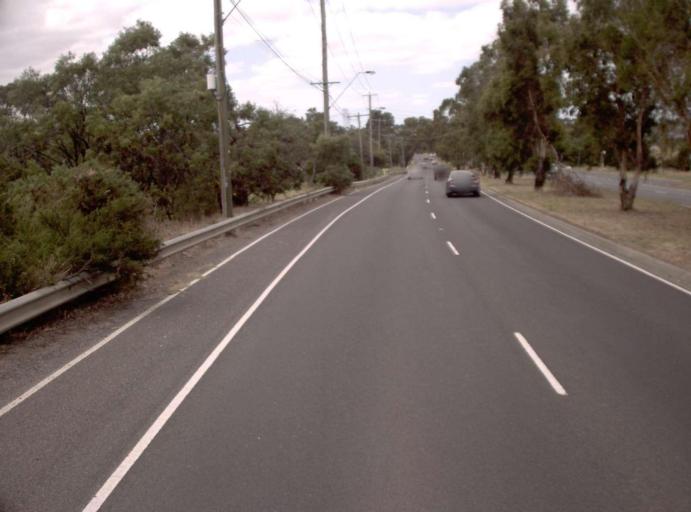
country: AU
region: Victoria
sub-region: Knox
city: Rowville
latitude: -37.9500
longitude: 145.2274
